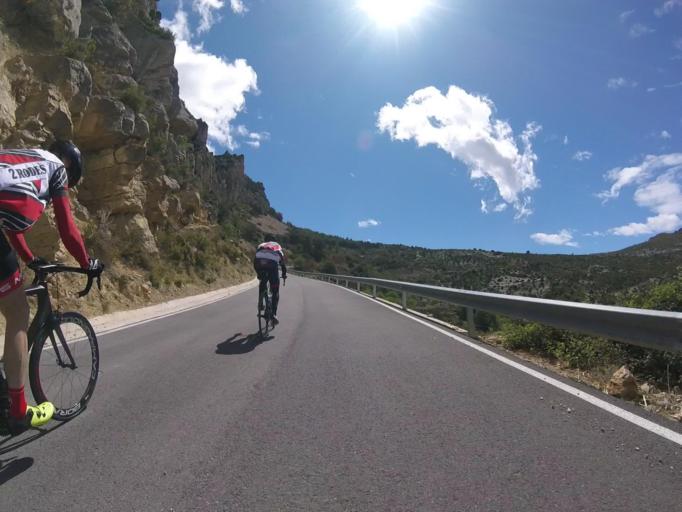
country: ES
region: Valencia
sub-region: Provincia de Castello
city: Sierra-Engarceran
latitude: 40.2841
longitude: -0.0344
